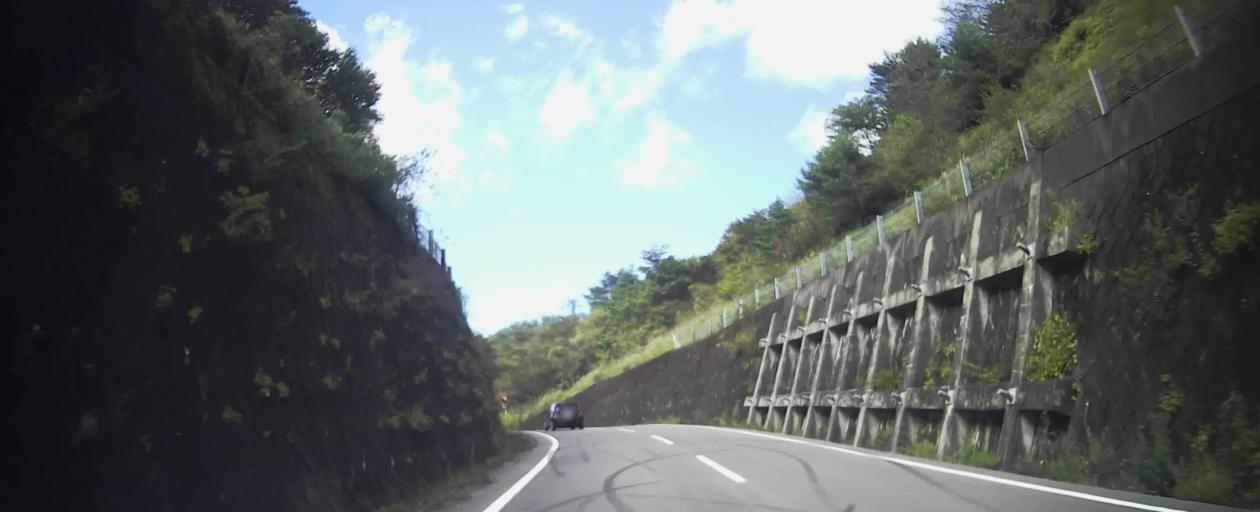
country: JP
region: Gunma
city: Shibukawa
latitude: 36.4684
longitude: 138.8867
